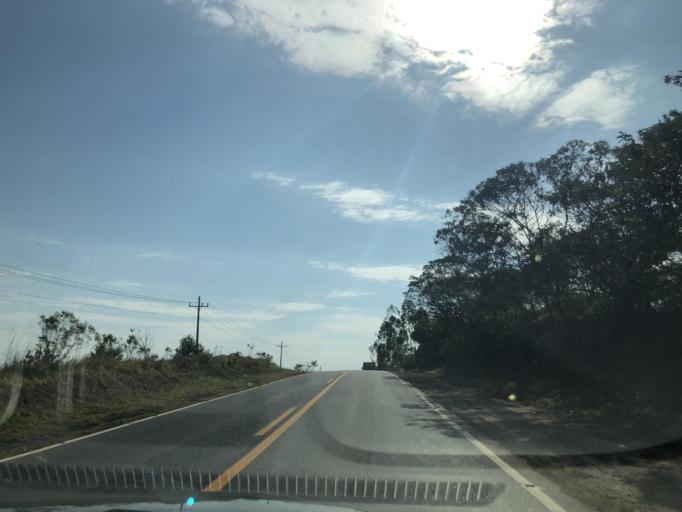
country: BR
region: Sao Paulo
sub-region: Pilar Do Sul
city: Pilar do Sul
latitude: -23.8137
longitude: -47.6839
